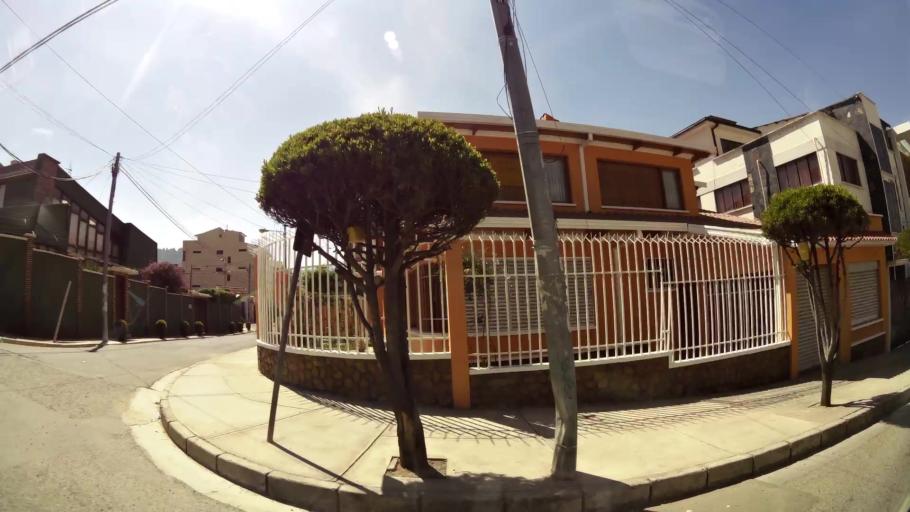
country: BO
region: La Paz
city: La Paz
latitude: -16.5338
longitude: -68.1031
